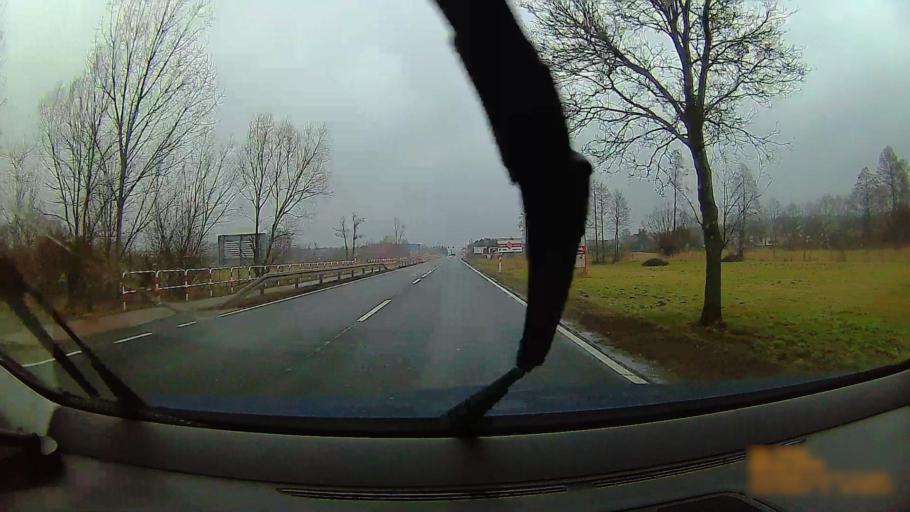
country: PL
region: Greater Poland Voivodeship
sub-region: Konin
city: Konin
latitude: 52.1733
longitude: 18.2728
